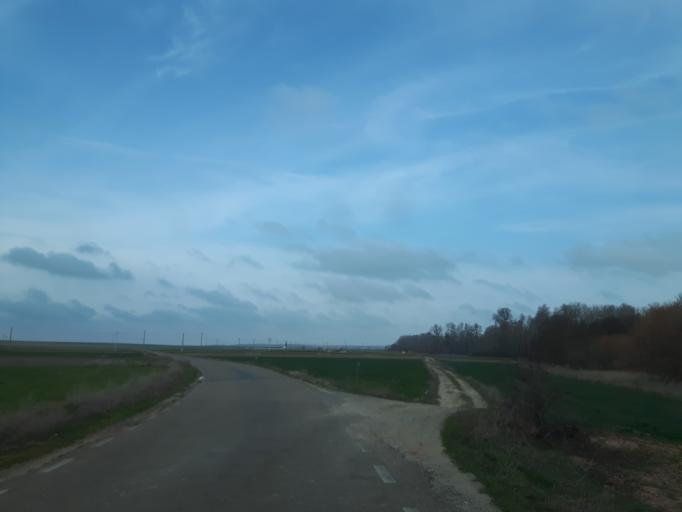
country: ES
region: Castille and Leon
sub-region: Provincia de Salamanca
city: Tordillos
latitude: 40.8596
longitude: -5.3600
